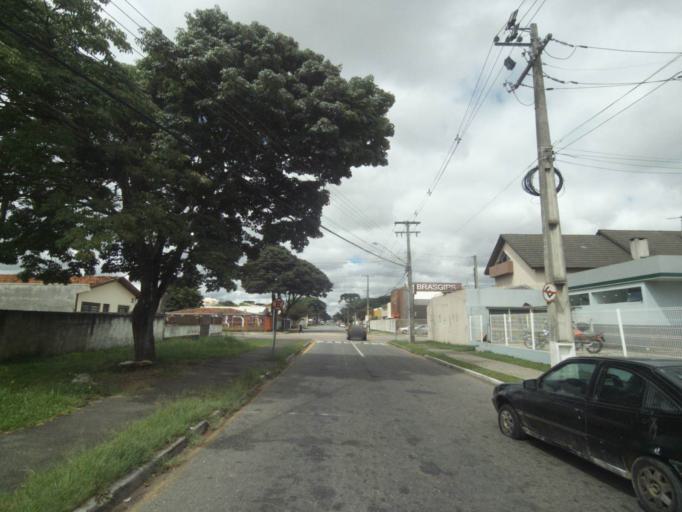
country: BR
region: Parana
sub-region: Curitiba
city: Curitiba
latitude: -25.4728
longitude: -49.2622
